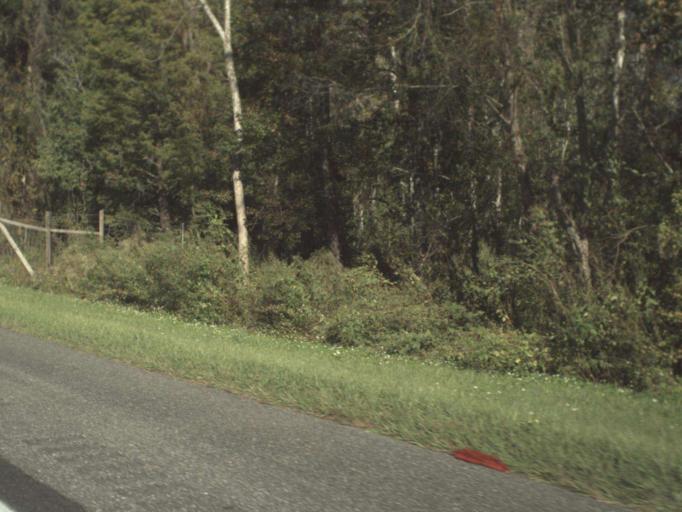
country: US
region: Florida
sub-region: Jefferson County
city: Monticello
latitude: 30.4668
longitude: -83.8018
